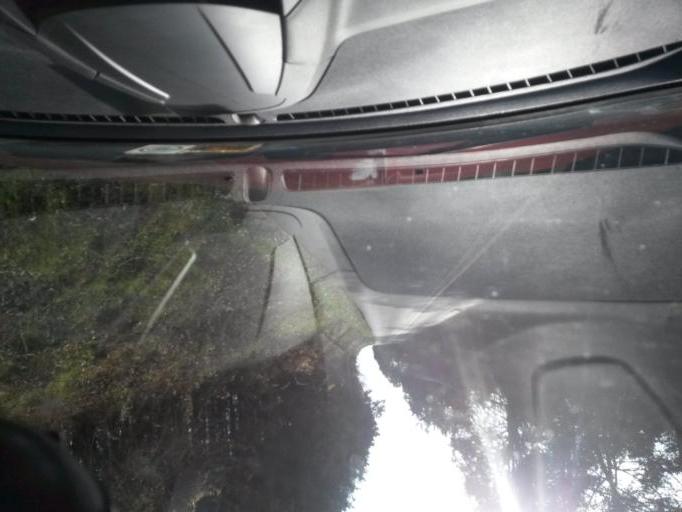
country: US
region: Virginia
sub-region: Botetourt County
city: Fincastle
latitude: 37.5260
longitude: -79.8819
